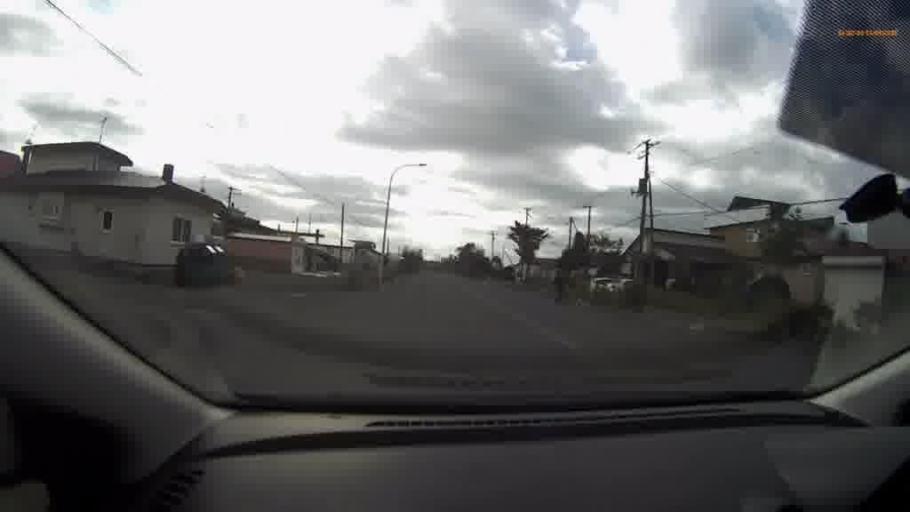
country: JP
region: Hokkaido
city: Kushiro
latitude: 42.9779
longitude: 144.1287
